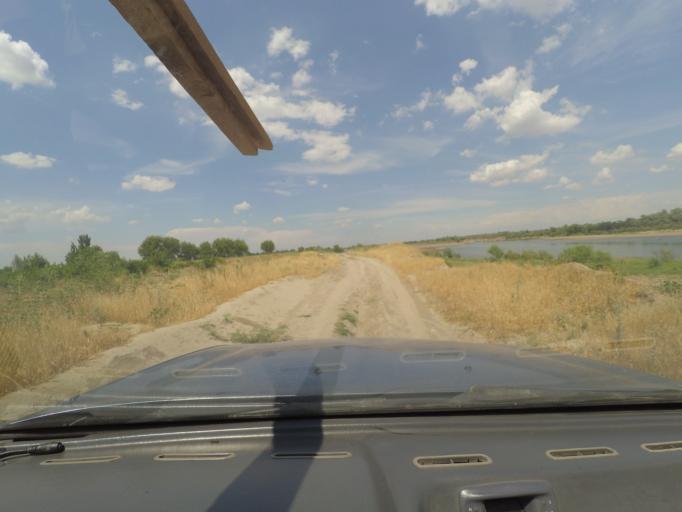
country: TJ
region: Viloyati Sughd
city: Buston
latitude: 40.5394
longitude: 69.0791
